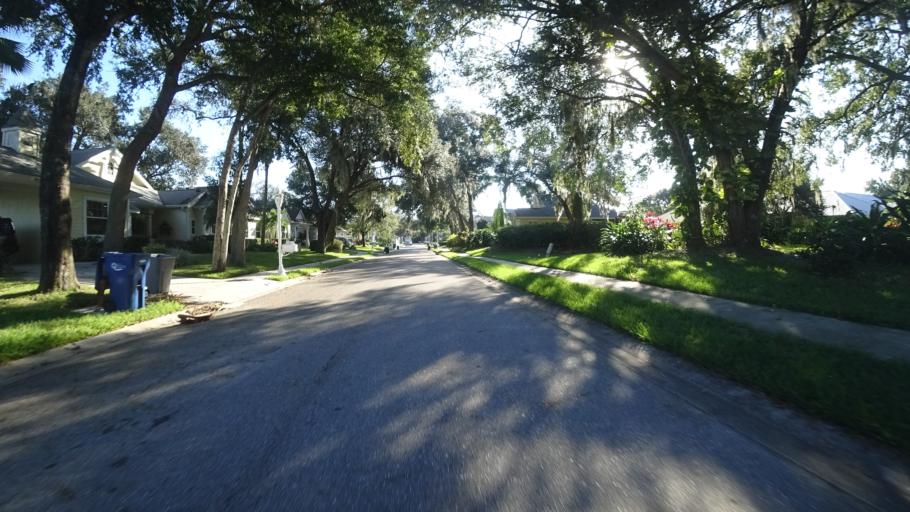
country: US
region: Florida
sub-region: Manatee County
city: Ellenton
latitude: 27.5003
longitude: -82.5057
